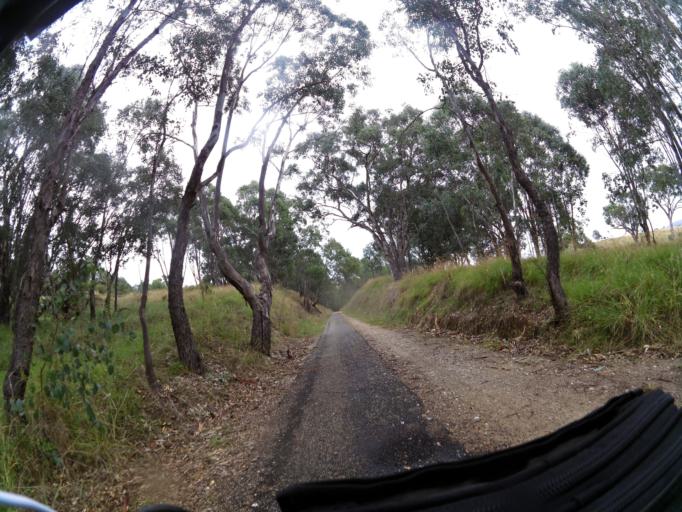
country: AU
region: New South Wales
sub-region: Albury Municipality
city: East Albury
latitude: -36.2242
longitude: 147.1287
